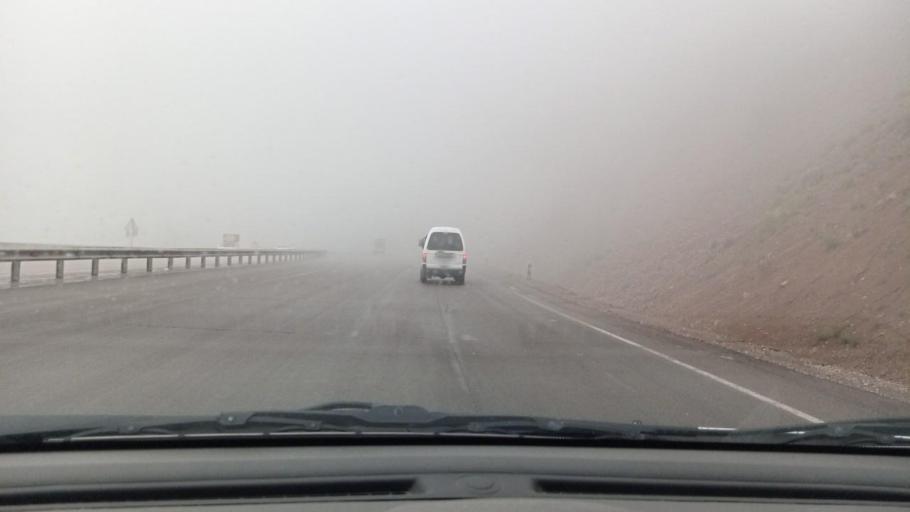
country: UZ
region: Toshkent
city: Angren
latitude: 41.1082
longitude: 70.5070
